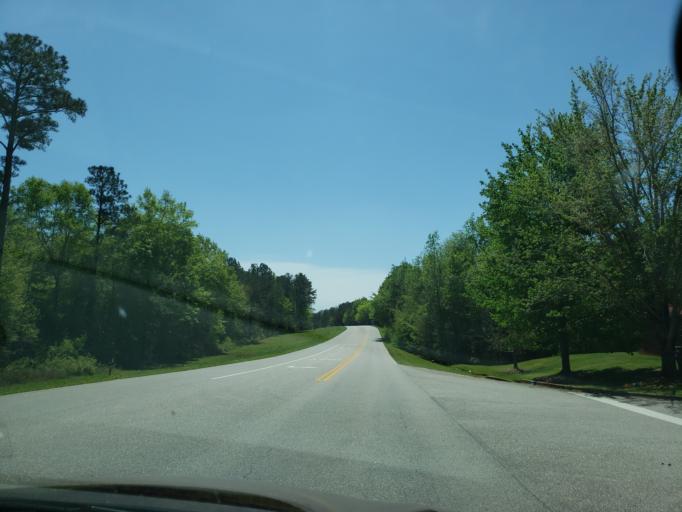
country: US
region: Alabama
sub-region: Lee County
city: Auburn
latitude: 32.6534
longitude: -85.5159
